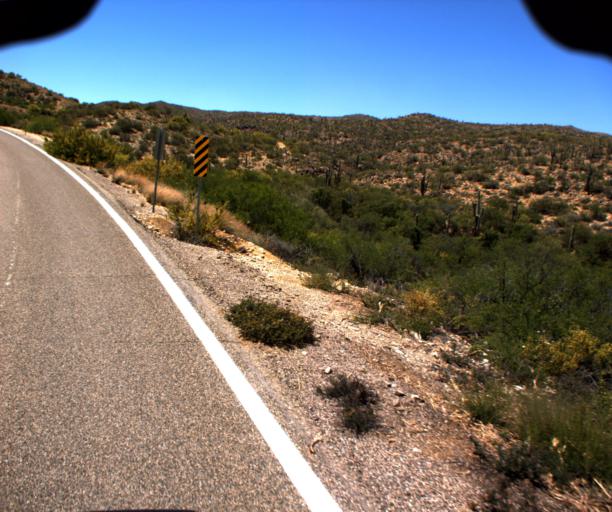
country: US
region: Arizona
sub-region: Yavapai County
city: Bagdad
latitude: 34.5184
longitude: -113.0930
